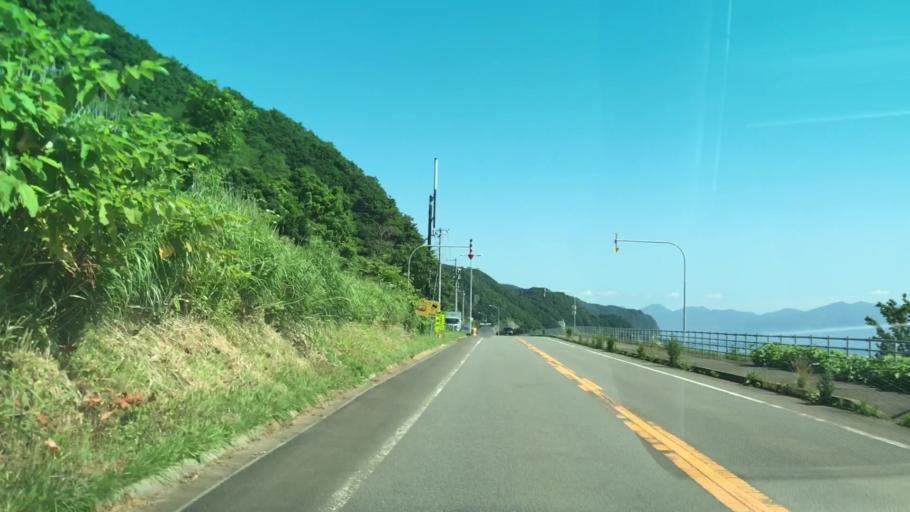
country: JP
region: Hokkaido
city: Iwanai
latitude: 43.1331
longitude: 140.4334
